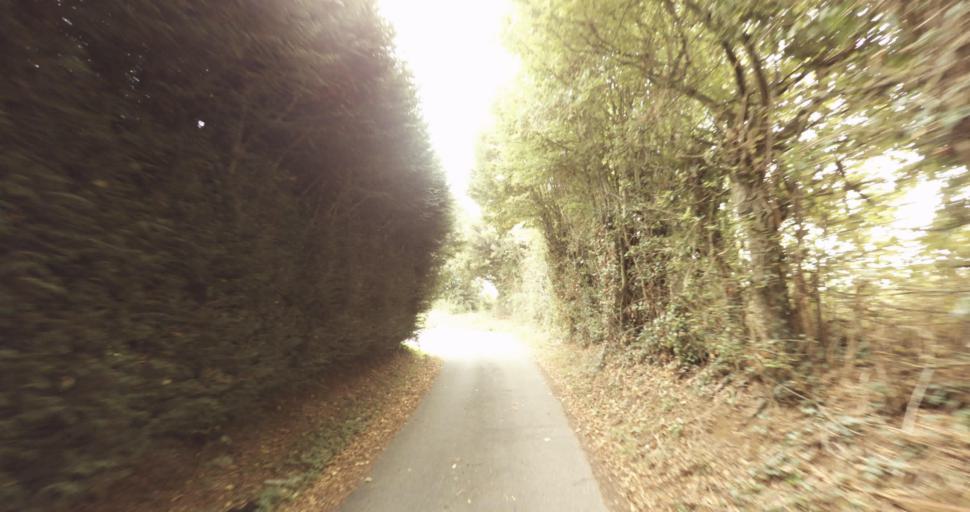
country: FR
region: Lower Normandy
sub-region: Departement de l'Orne
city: Sainte-Gauburge-Sainte-Colombe
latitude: 48.7301
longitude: 0.3582
